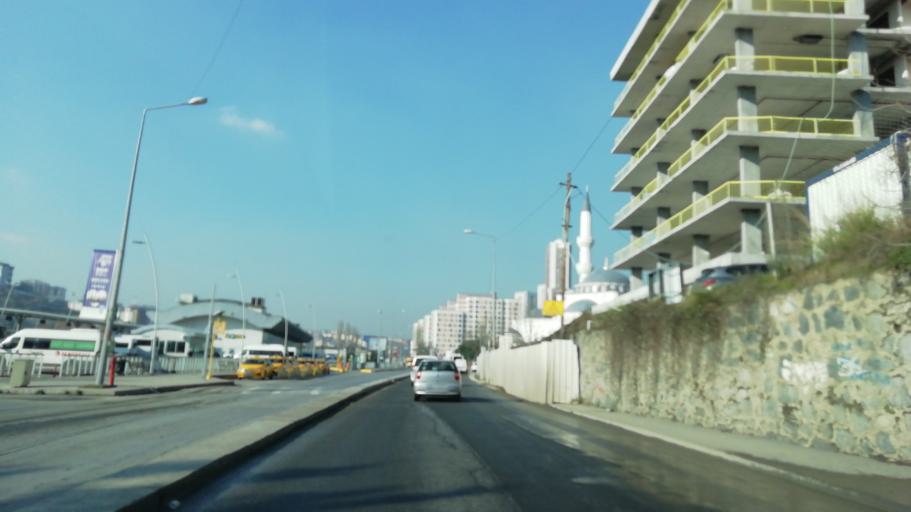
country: TR
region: Istanbul
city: Sisli
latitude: 41.0880
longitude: 28.9472
